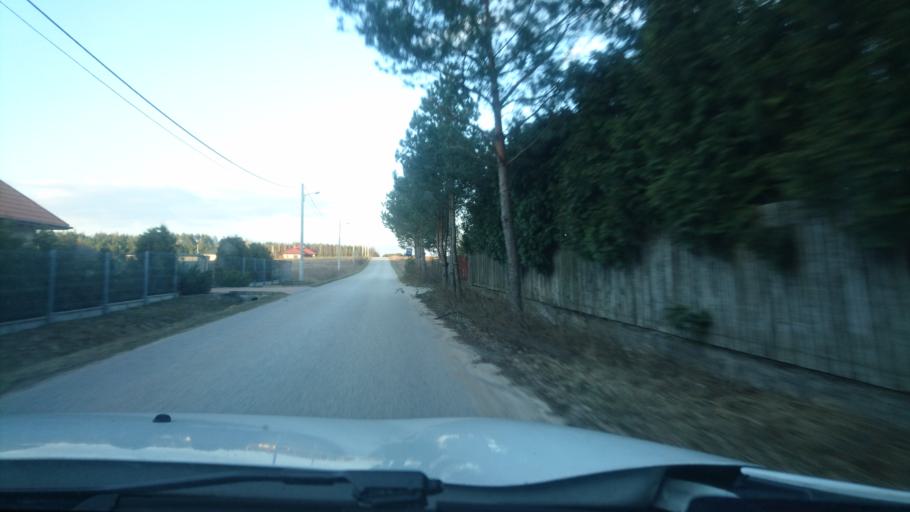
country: PL
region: Swietokrzyskie
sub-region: Powiat kielecki
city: Morawica
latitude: 50.7669
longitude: 20.6900
